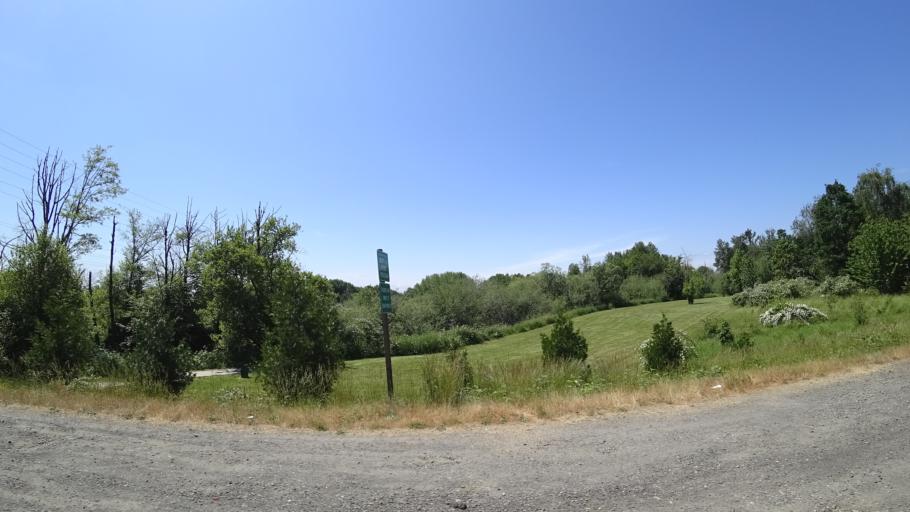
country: US
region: Oregon
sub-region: Multnomah County
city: Fairview
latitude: 45.5566
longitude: -122.4359
